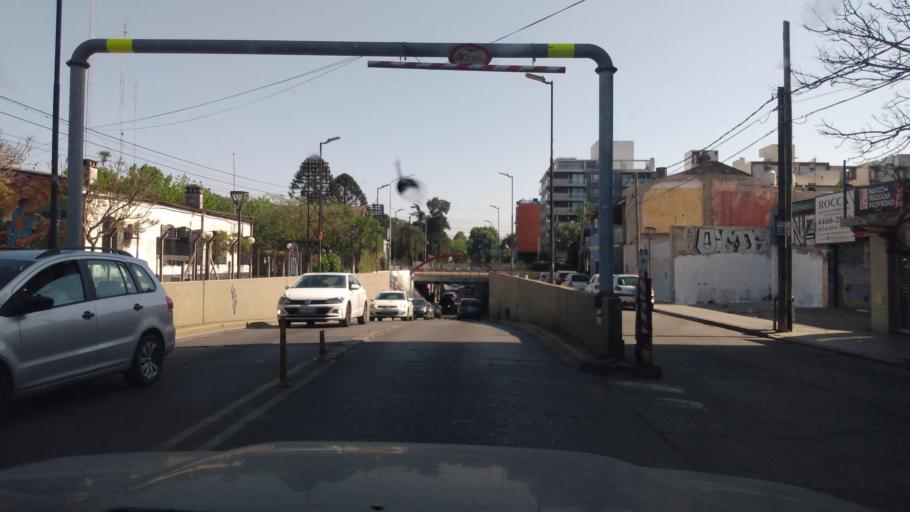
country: AR
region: Buenos Aires
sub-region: Partido de Moron
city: Moron
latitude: -34.6458
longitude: -58.5947
